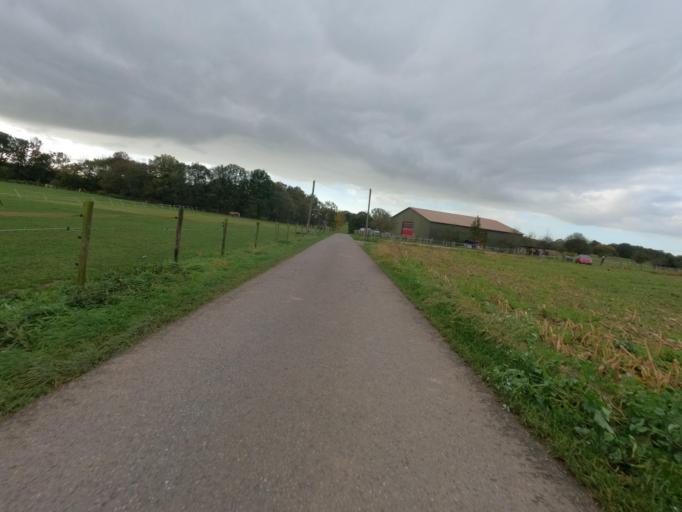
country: DE
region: North Rhine-Westphalia
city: Huckelhoven
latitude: 51.0554
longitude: 6.2733
